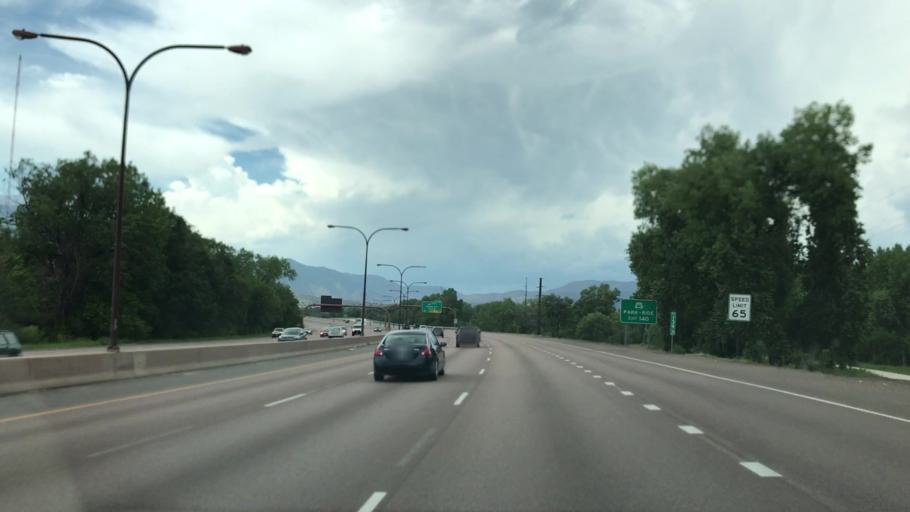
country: US
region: Colorado
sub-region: El Paso County
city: Colorado Springs
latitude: 38.8125
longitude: -104.8122
